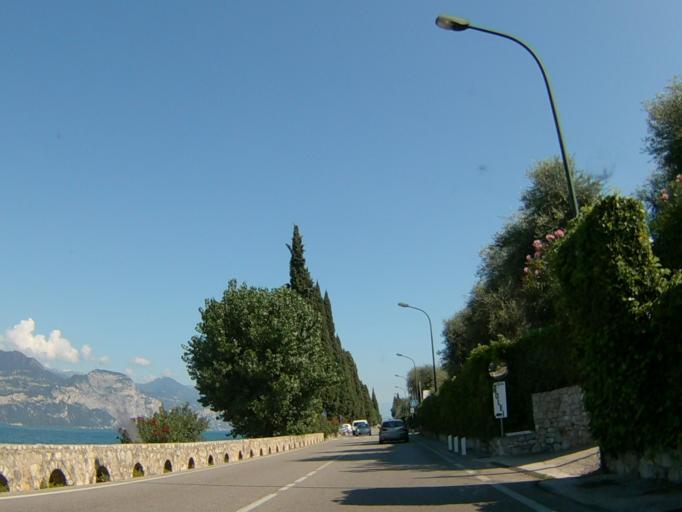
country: IT
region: Veneto
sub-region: Provincia di Verona
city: Brenzone
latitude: 45.6746
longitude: 10.7385
